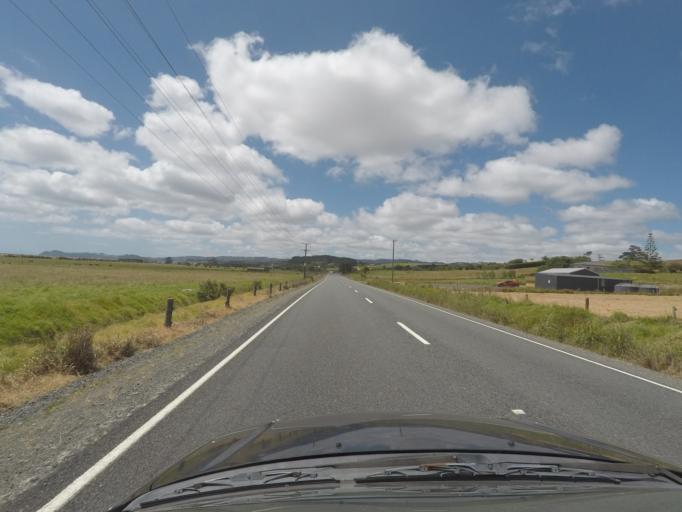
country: NZ
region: Northland
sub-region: Whangarei
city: Ruakaka
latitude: -36.0075
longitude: 174.4797
